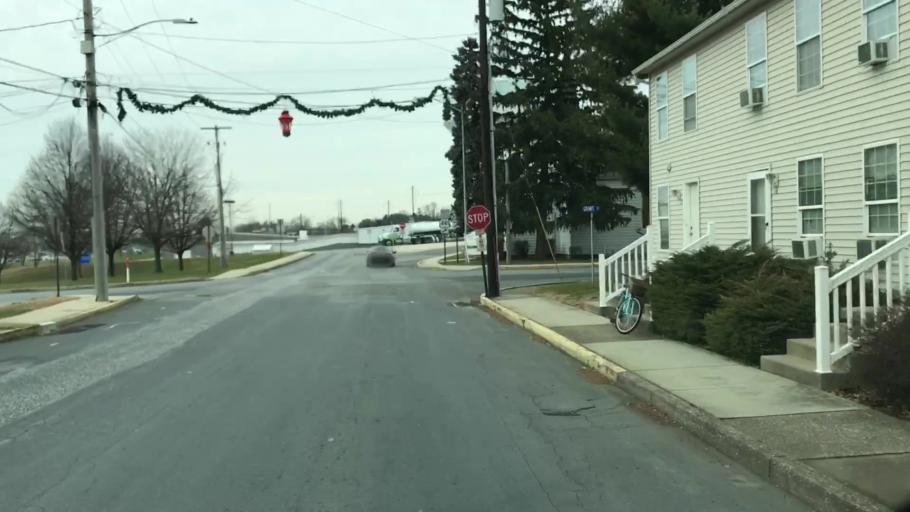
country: US
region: Pennsylvania
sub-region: Dauphin County
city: Middletown
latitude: 40.1946
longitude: -76.7384
